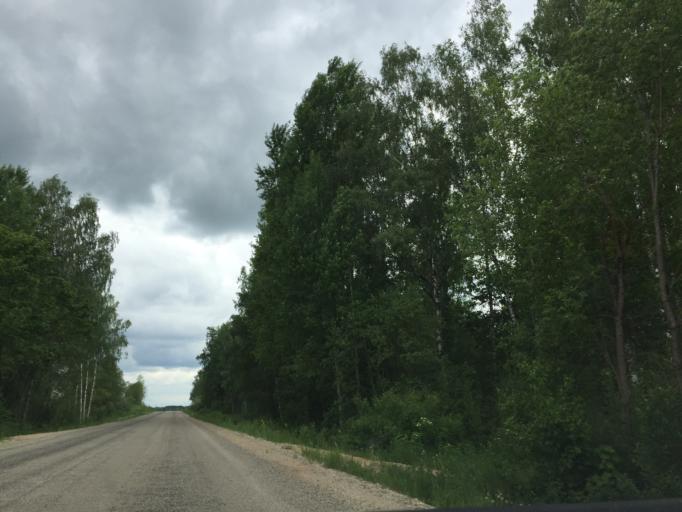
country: LV
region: Dagda
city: Dagda
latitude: 56.0698
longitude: 27.5566
